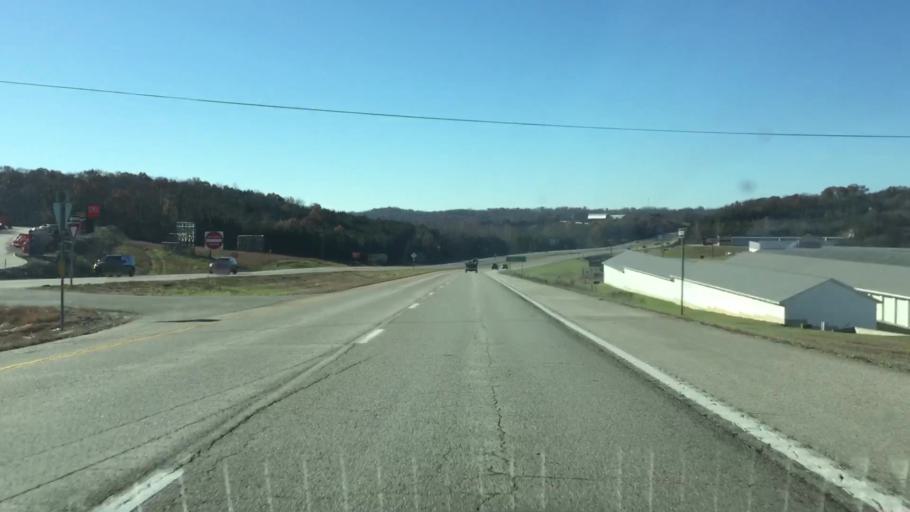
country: US
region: Missouri
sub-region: Cole County
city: Wardsville
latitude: 38.5319
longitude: -92.2195
